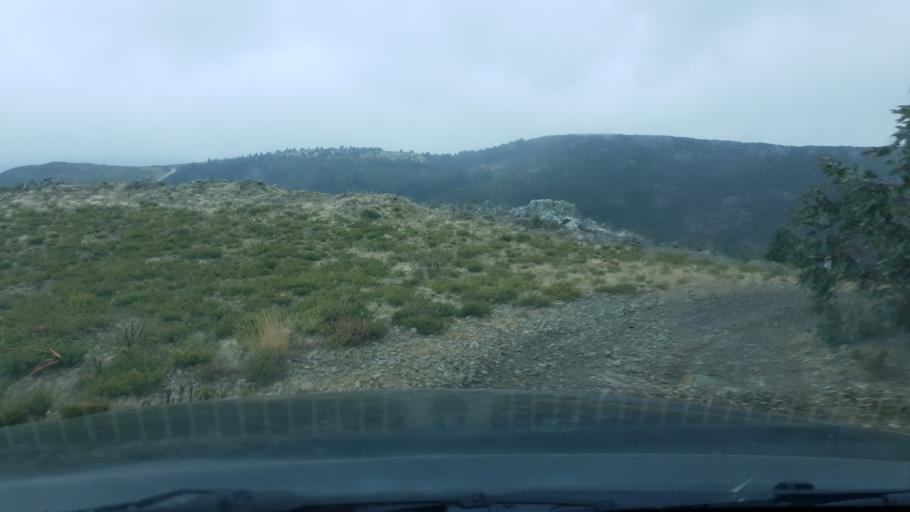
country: PT
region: Viseu
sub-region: Sao Pedro do Sul
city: Sao Pedro do Sul
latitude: 40.8587
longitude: -8.0976
